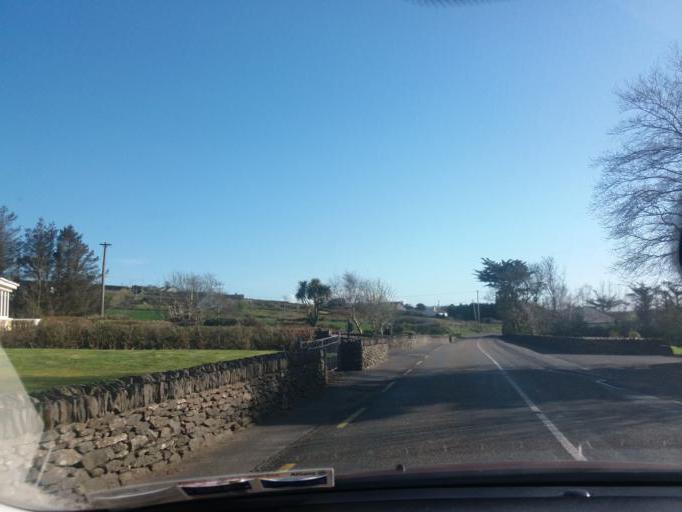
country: IE
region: Munster
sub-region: Ciarrai
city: Dingle
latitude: 52.1572
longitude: -10.2853
